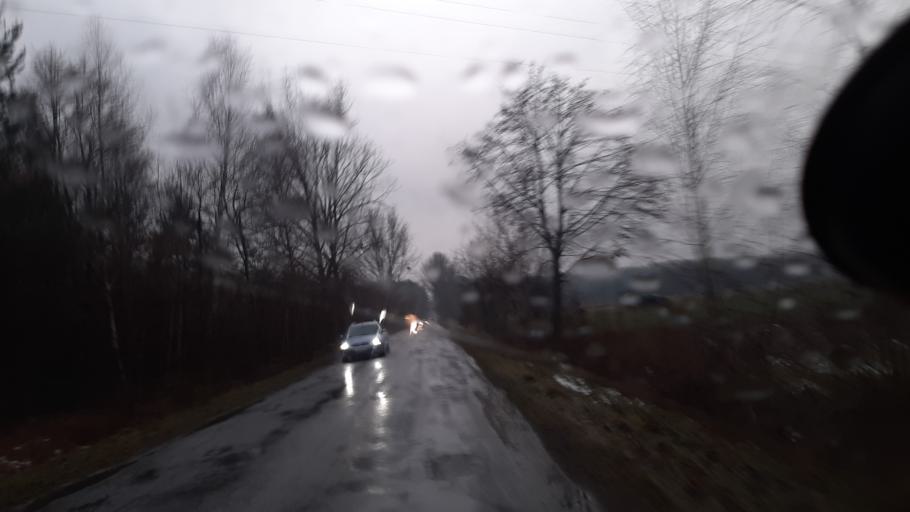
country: PL
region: Lublin Voivodeship
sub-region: Powiat lubartowski
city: Firlej
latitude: 51.5209
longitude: 22.4979
